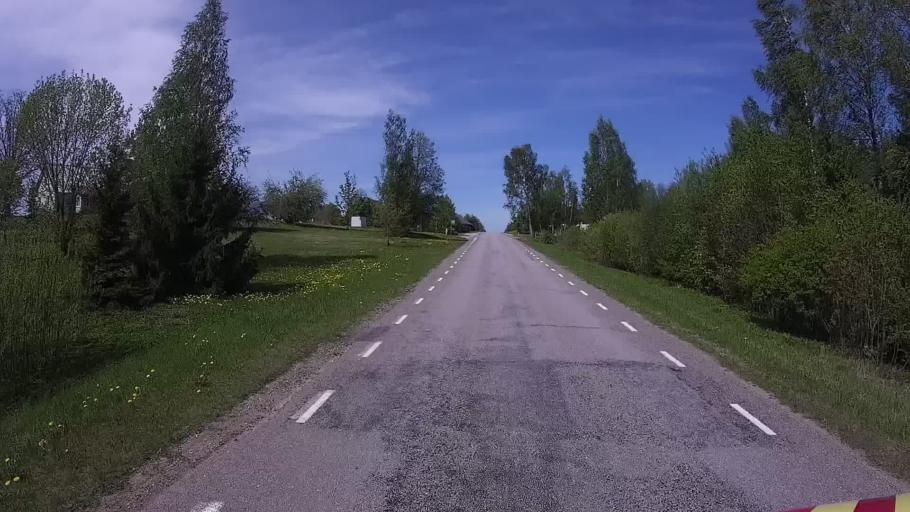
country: EE
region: Vorumaa
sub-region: Antsla vald
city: Vana-Antsla
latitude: 57.6275
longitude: 26.3442
